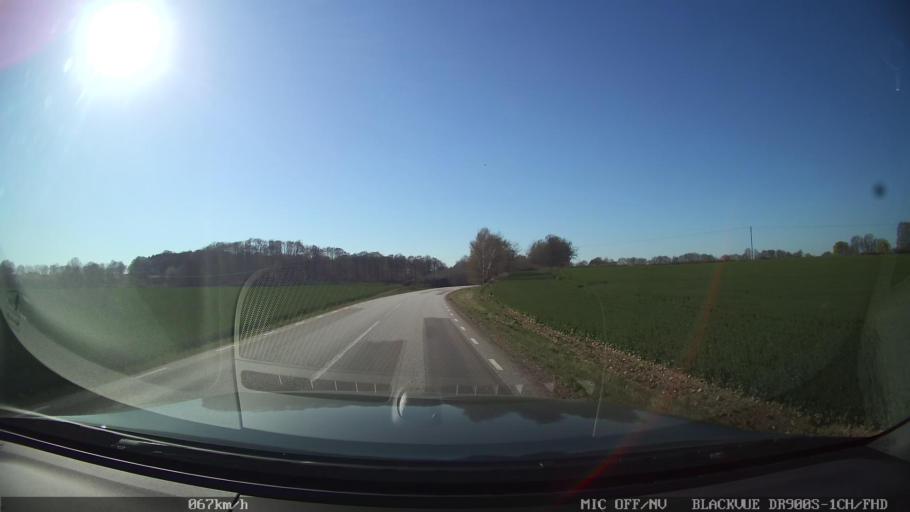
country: SE
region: Skane
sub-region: Klippans Kommun
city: Ljungbyhed
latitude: 55.9656
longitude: 13.2196
